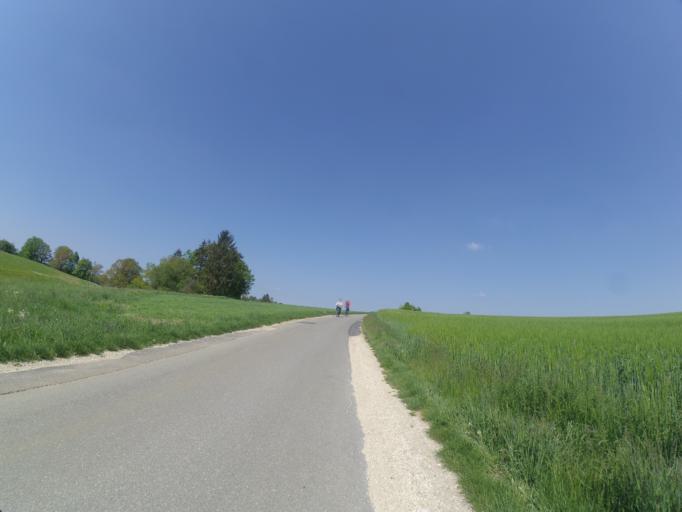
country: DE
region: Baden-Wuerttemberg
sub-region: Tuebingen Region
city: Berghulen
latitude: 48.4764
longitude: 9.8238
